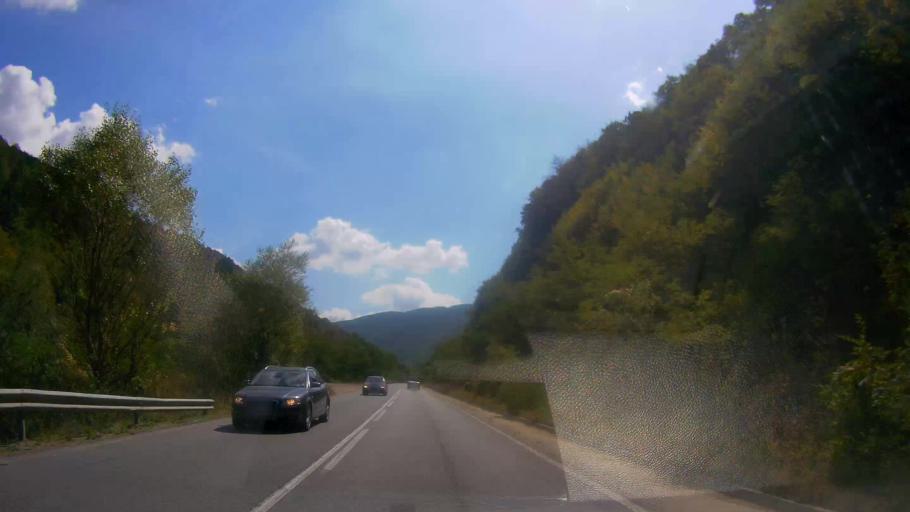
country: BG
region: Stara Zagora
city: Gurkovo
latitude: 42.7248
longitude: 25.7128
